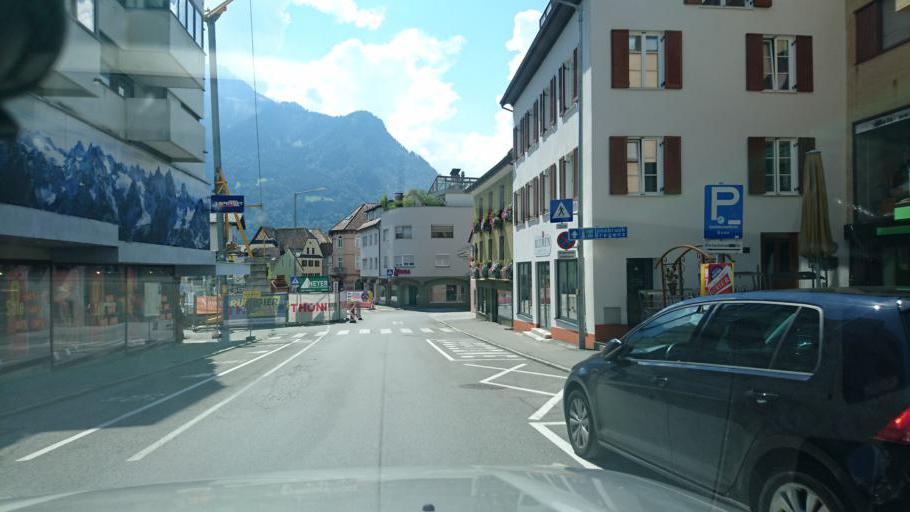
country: AT
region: Vorarlberg
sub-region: Politischer Bezirk Bludenz
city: Bludenz
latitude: 47.1549
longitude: 9.8199
